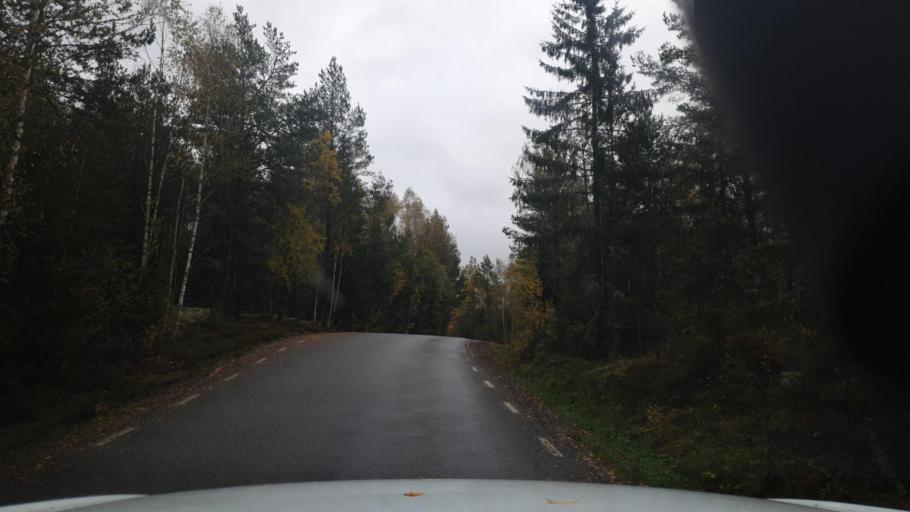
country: SE
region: Vaermland
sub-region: Karlstads Kommun
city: Valberg
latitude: 59.4161
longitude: 13.1269
